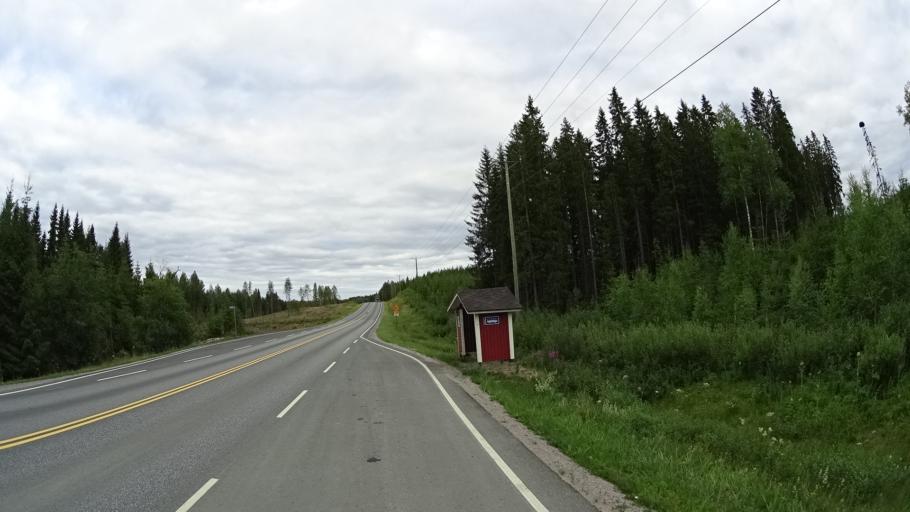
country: FI
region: Satakunta
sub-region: Pohjois-Satakunta
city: Jaemijaervi
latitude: 61.7784
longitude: 22.8622
